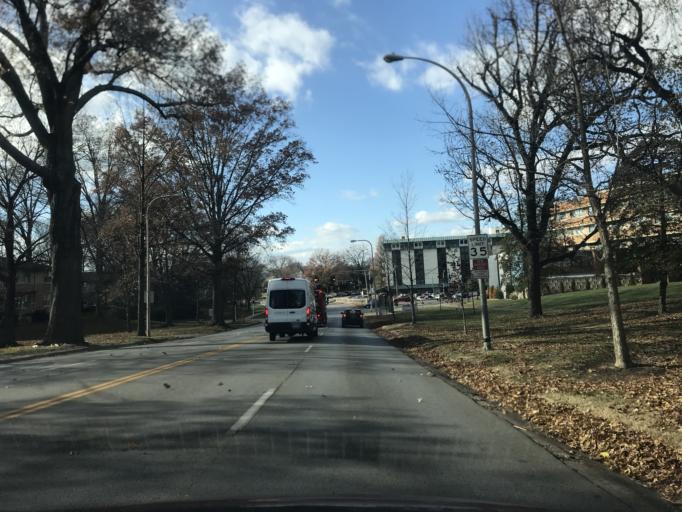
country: US
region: Kentucky
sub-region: Jefferson County
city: Audubon Park
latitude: 38.2253
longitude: -85.7253
